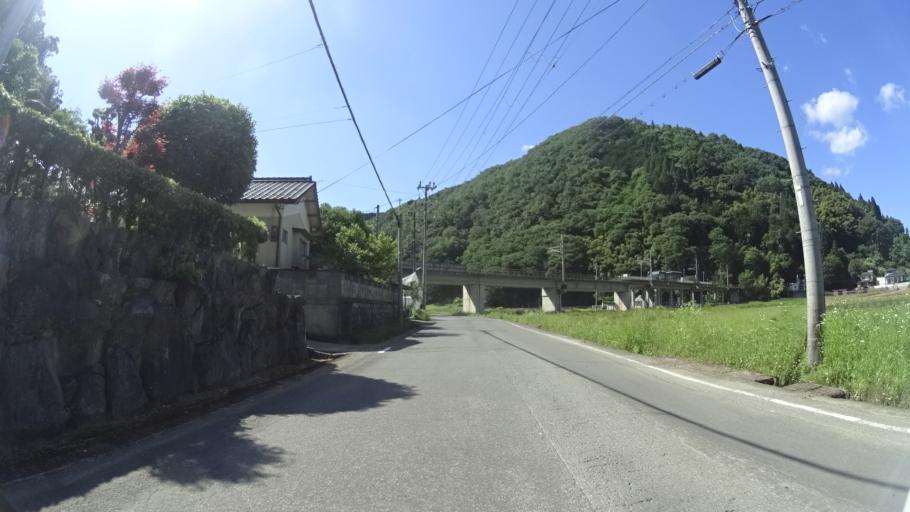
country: JP
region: Kyoto
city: Fukuchiyama
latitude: 35.3579
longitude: 135.1117
